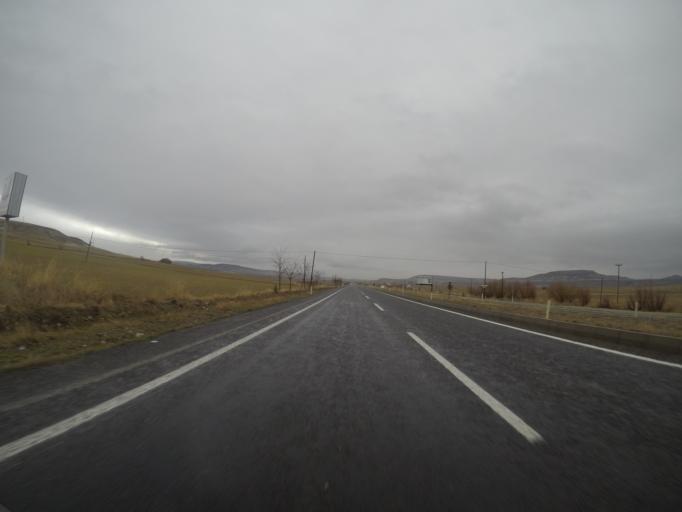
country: TR
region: Nevsehir
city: Urgub
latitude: 38.7163
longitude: 34.9369
